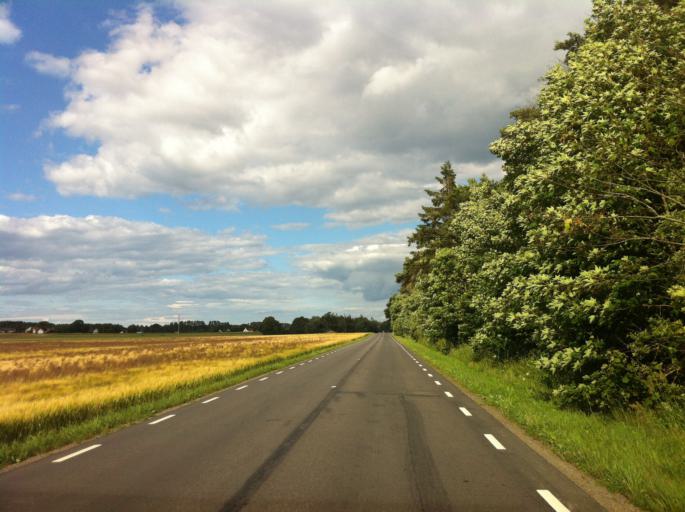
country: SE
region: Skane
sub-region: Simrishamns Kommun
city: Simrishamn
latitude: 55.4325
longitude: 14.2248
